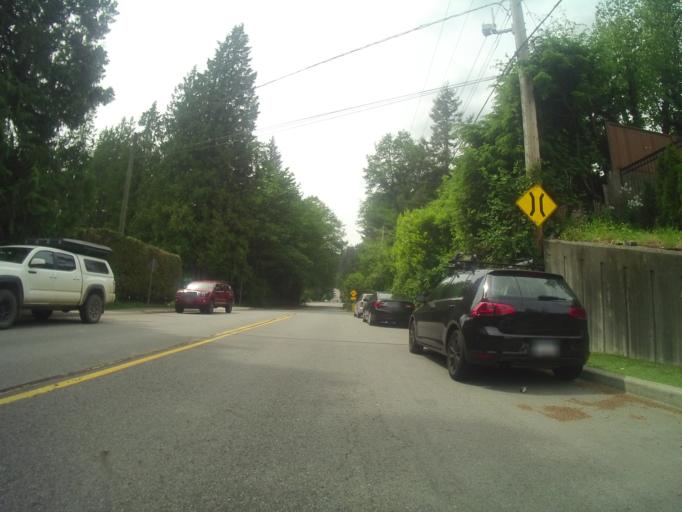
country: CA
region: British Columbia
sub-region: Fraser Valley Regional District
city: North Vancouver
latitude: 49.3479
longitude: -123.0311
